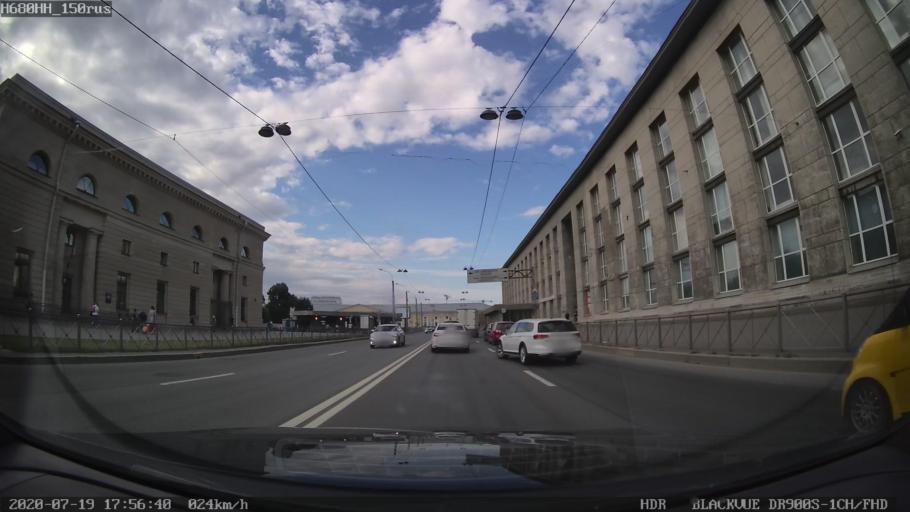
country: RU
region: St.-Petersburg
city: Admiralteisky
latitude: 59.9070
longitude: 30.3005
